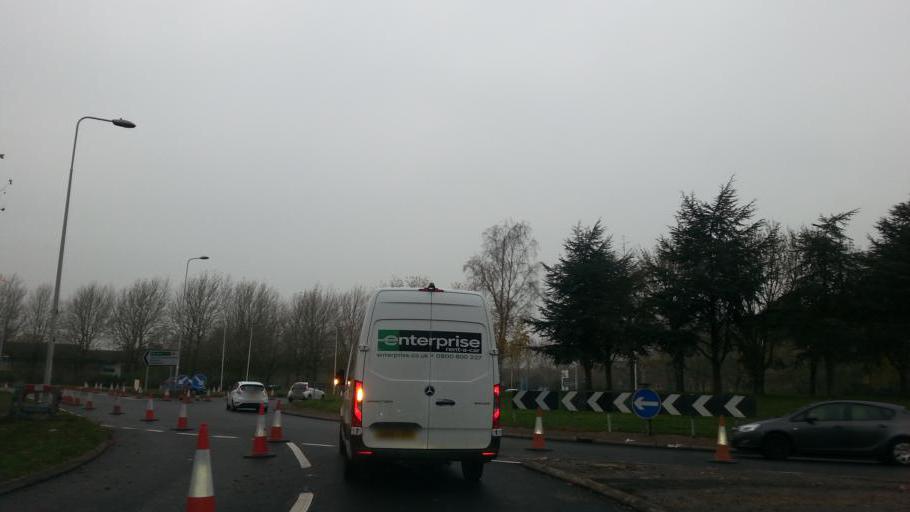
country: GB
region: England
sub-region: Peterborough
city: Castor
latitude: 52.5516
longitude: -0.3121
